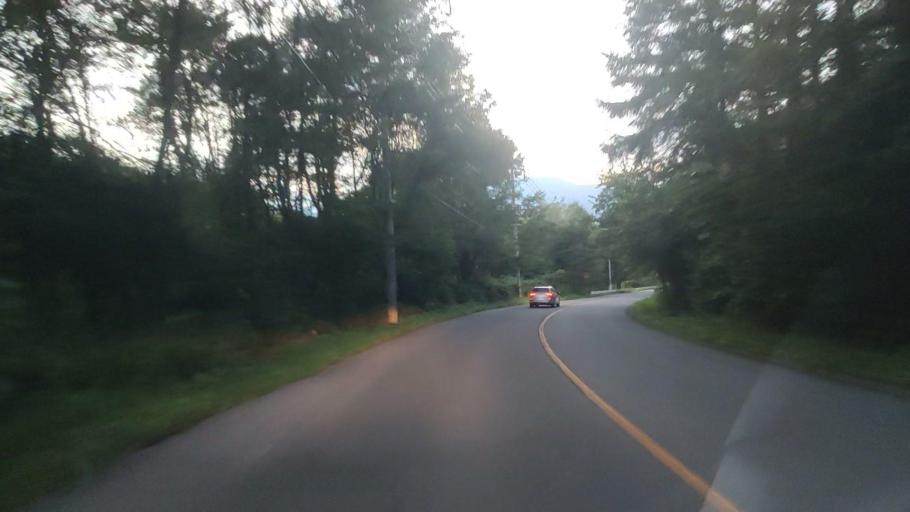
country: JP
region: Gunma
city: Nakanojomachi
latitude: 36.5331
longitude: 138.6095
